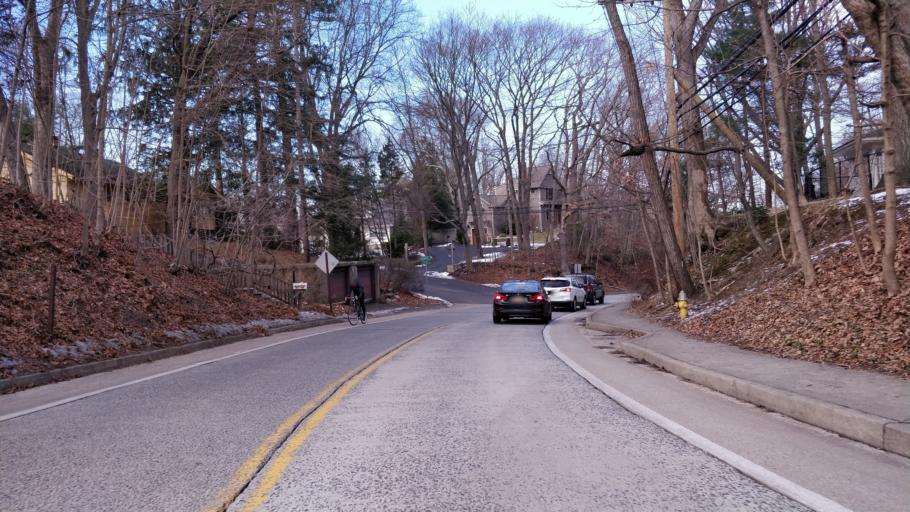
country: US
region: New York
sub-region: Suffolk County
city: Northport
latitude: 40.8971
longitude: -73.3421
